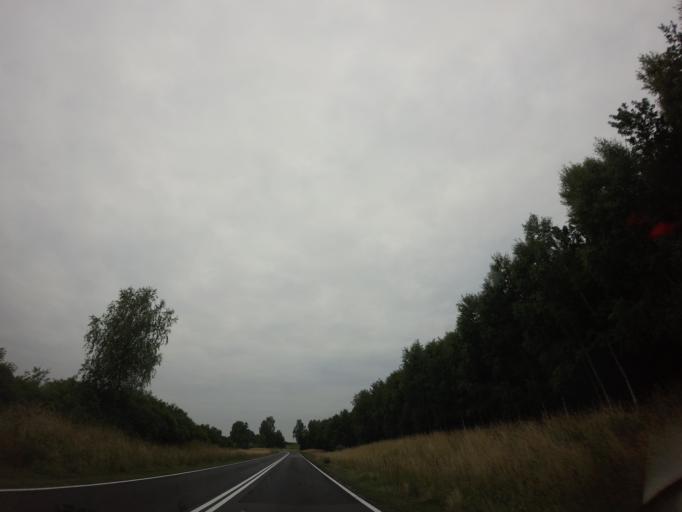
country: PL
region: West Pomeranian Voivodeship
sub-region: Powiat walecki
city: Miroslawiec
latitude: 53.3314
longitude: 16.0512
